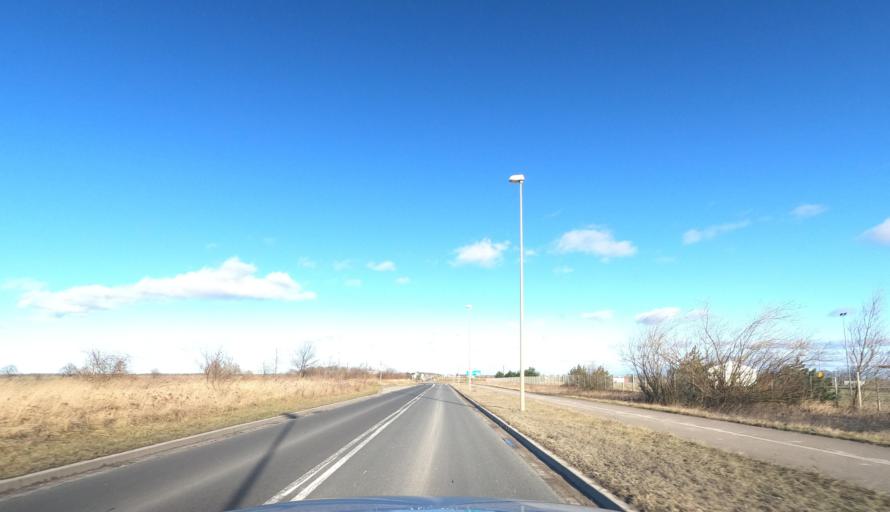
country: PL
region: West Pomeranian Voivodeship
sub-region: Powiat pyrzycki
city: Warnice
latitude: 53.3040
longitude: 14.9719
